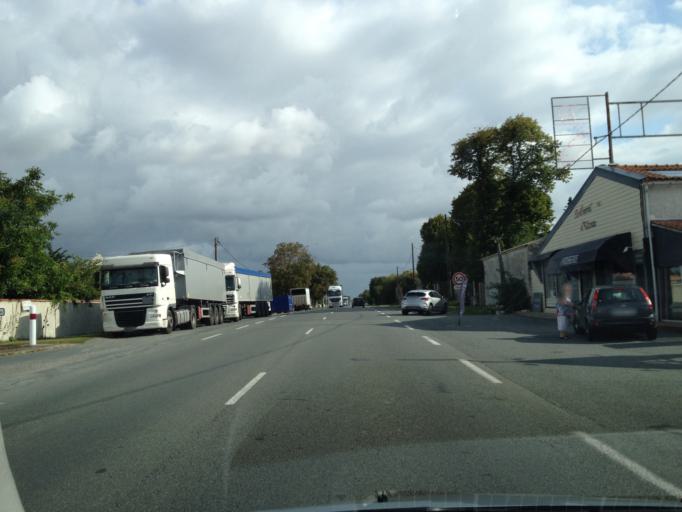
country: FR
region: Poitou-Charentes
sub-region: Departement de la Charente-Maritime
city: Sainte-Soulle
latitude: 46.2077
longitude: -1.0266
